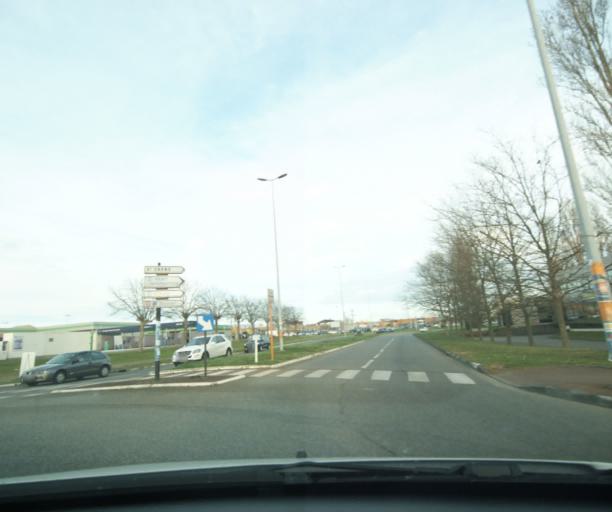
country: FR
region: Midi-Pyrenees
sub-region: Departement de la Haute-Garonne
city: Ramonville-Saint-Agne
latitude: 43.5499
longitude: 1.5039
